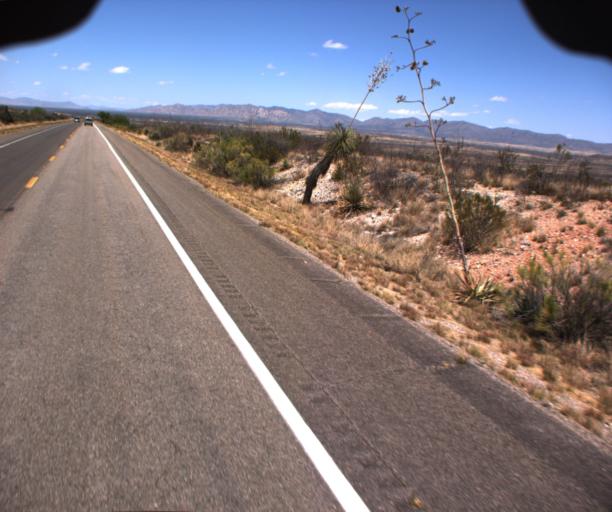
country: US
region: Arizona
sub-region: Cochise County
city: Tombstone
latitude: 31.6804
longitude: -110.0330
